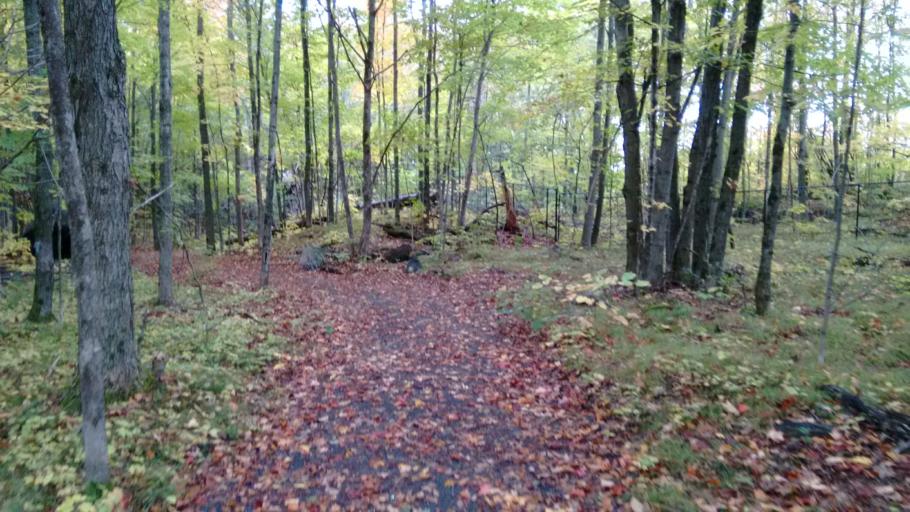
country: CA
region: Ontario
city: Bells Corners
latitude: 45.3552
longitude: -76.0422
